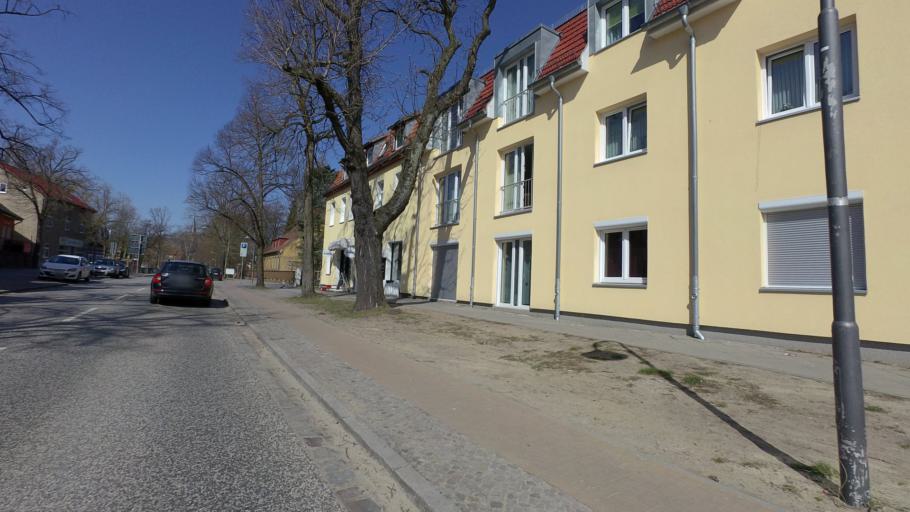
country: DE
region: Brandenburg
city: Birkenwerder
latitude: 52.6892
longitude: 13.2810
